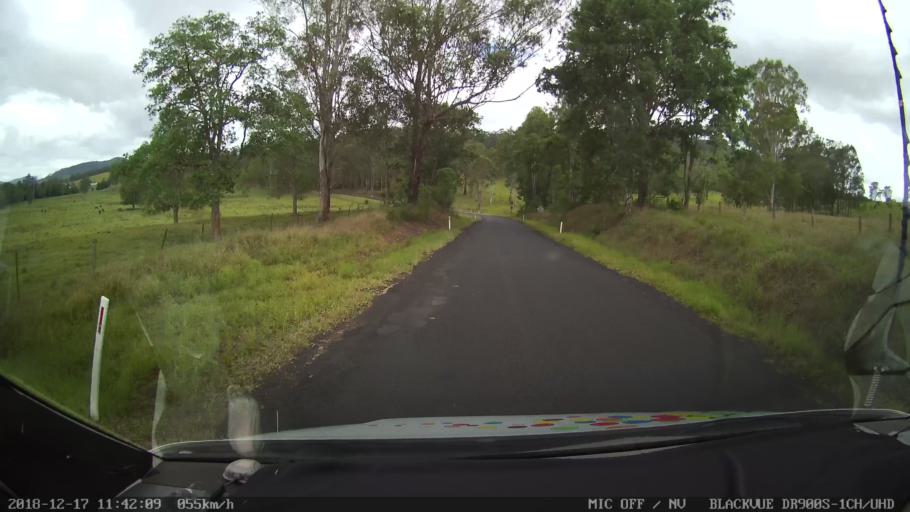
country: AU
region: New South Wales
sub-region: Kyogle
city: Kyogle
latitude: -28.6697
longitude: 152.5886
